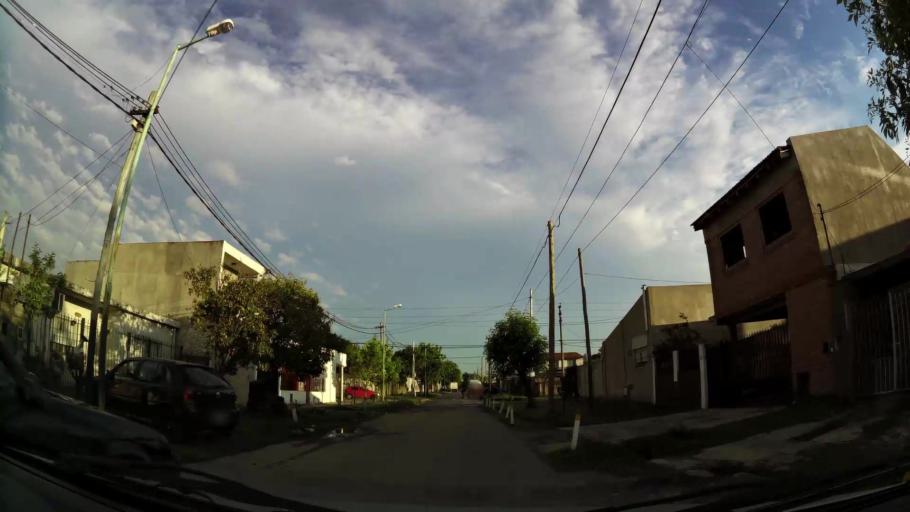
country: AR
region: Buenos Aires
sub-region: Partido de Almirante Brown
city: Adrogue
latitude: -34.7614
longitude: -58.3543
